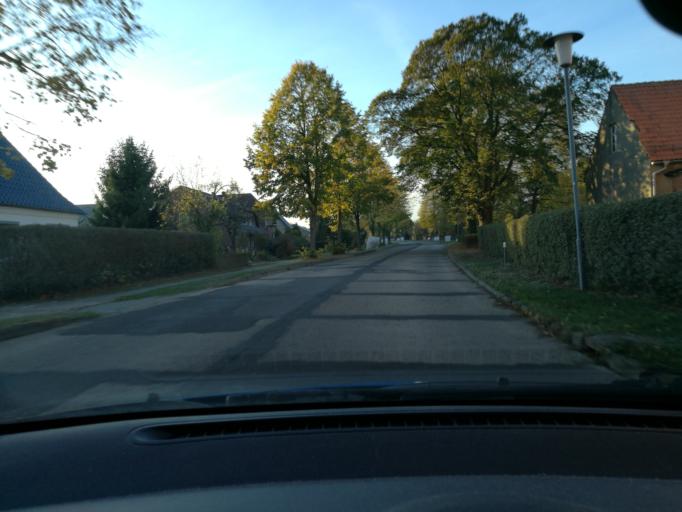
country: DE
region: Brandenburg
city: Weisen
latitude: 53.0796
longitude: 11.8029
